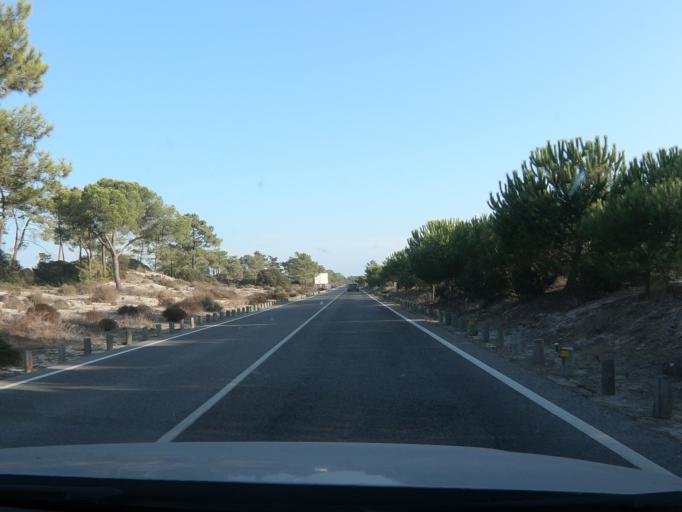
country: PT
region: Setubal
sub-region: Setubal
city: Setubal
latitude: 38.4806
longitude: -8.8905
